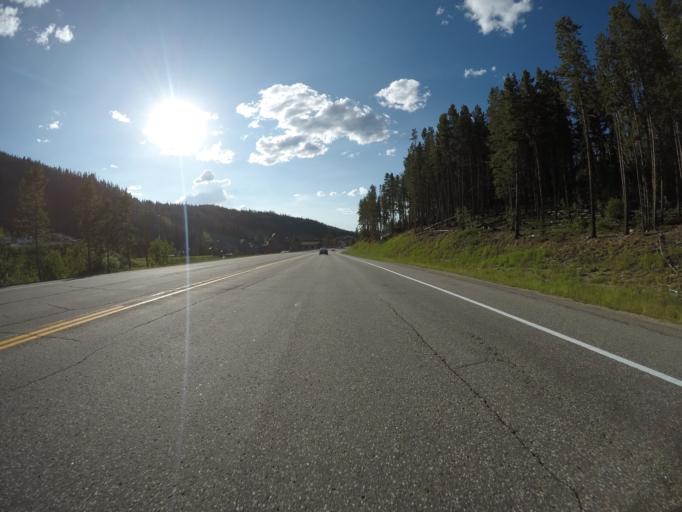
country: US
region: Colorado
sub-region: Grand County
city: Fraser
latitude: 39.8834
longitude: -105.7578
